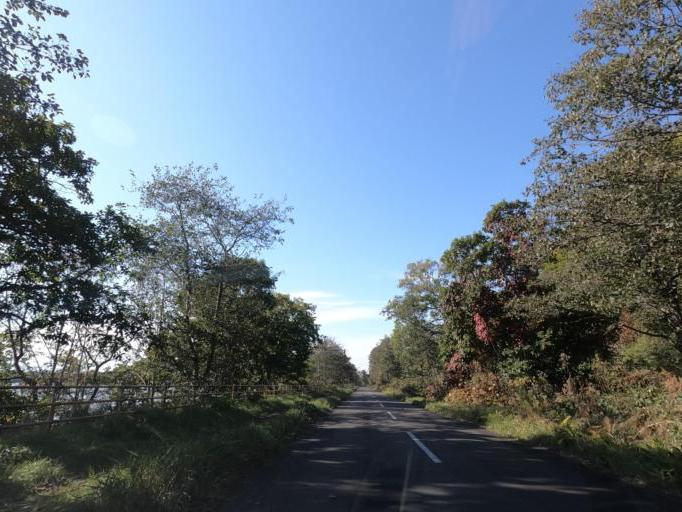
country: JP
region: Hokkaido
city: Obihiro
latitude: 42.6080
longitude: 143.5488
